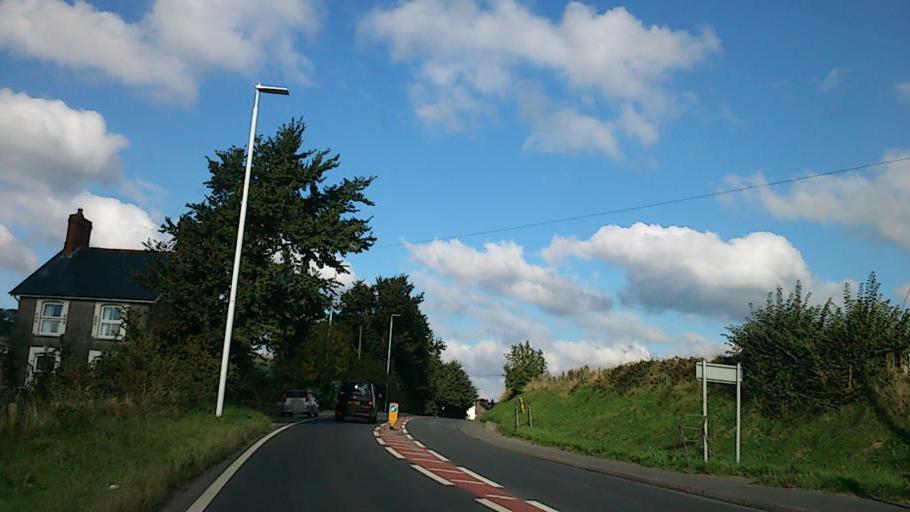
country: GB
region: Wales
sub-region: County of Ceredigion
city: Bow Street
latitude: 52.4392
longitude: -4.0292
